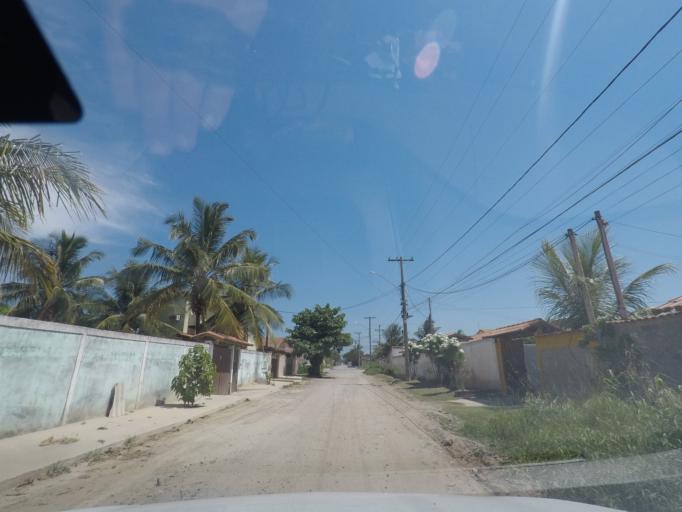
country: BR
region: Rio de Janeiro
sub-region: Marica
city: Marica
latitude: -22.9560
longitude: -42.9568
